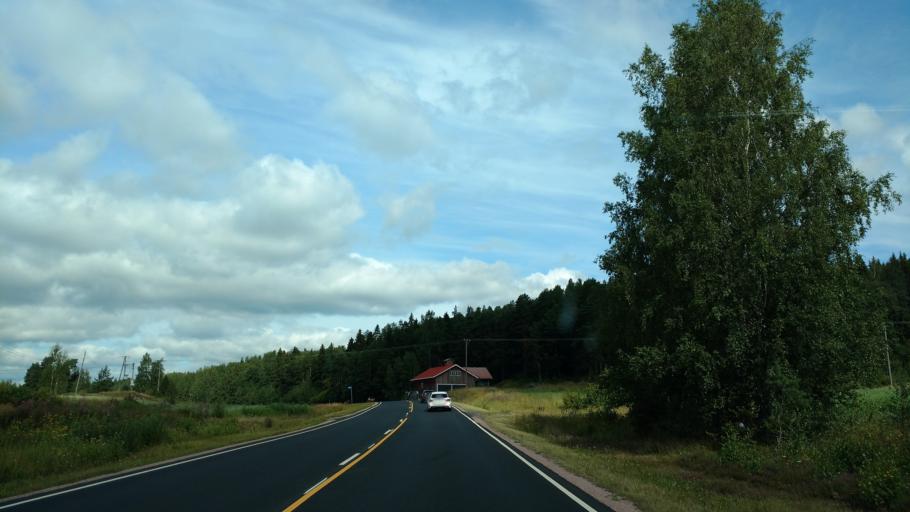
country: FI
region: Varsinais-Suomi
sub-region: Salo
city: Saerkisalo
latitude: 60.1825
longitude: 22.8979
